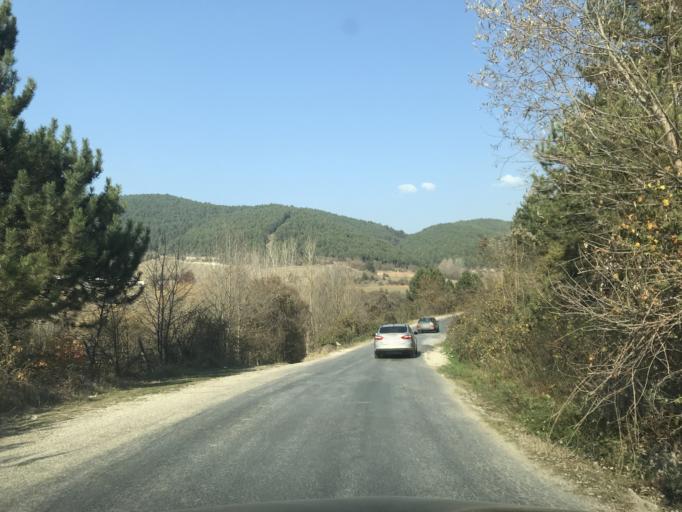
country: TR
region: Bolu
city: Bolu
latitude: 40.7876
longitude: 31.6363
